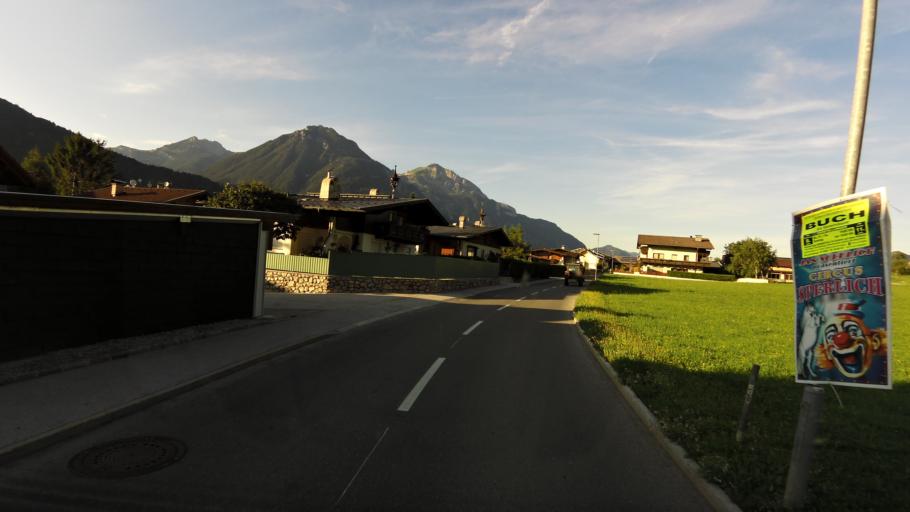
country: AT
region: Tyrol
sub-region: Politischer Bezirk Schwaz
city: Gallzein
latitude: 47.3785
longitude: 11.7701
